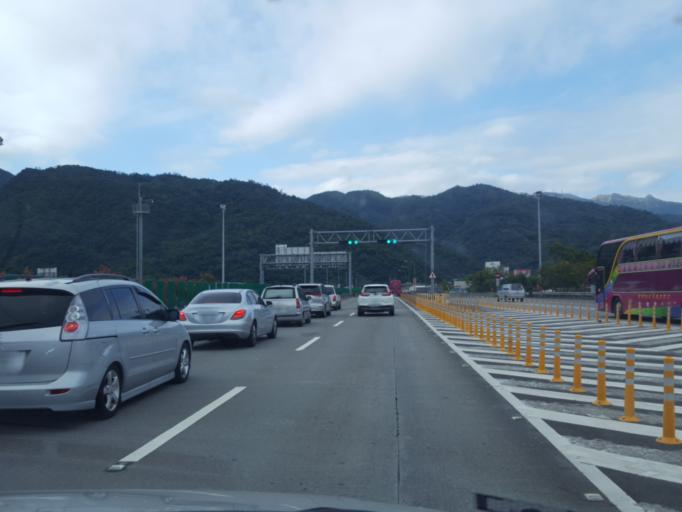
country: TW
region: Taiwan
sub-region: Yilan
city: Yilan
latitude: 24.8348
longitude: 121.7906
